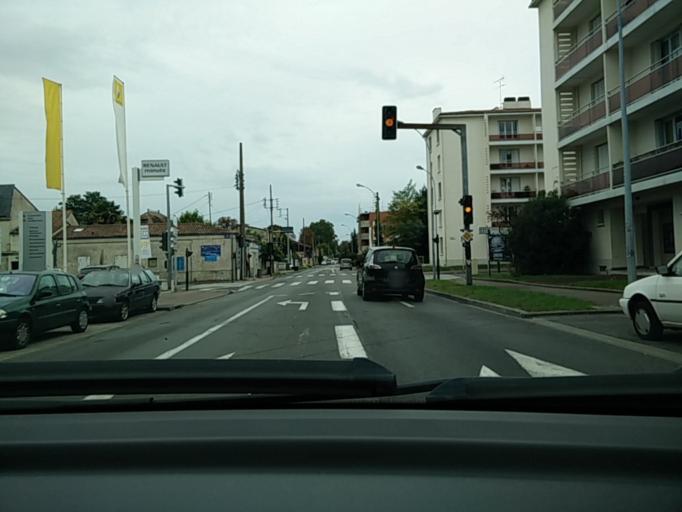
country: FR
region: Aquitaine
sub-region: Departement de la Gironde
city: Le Bouscat
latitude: 44.8650
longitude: -0.6047
